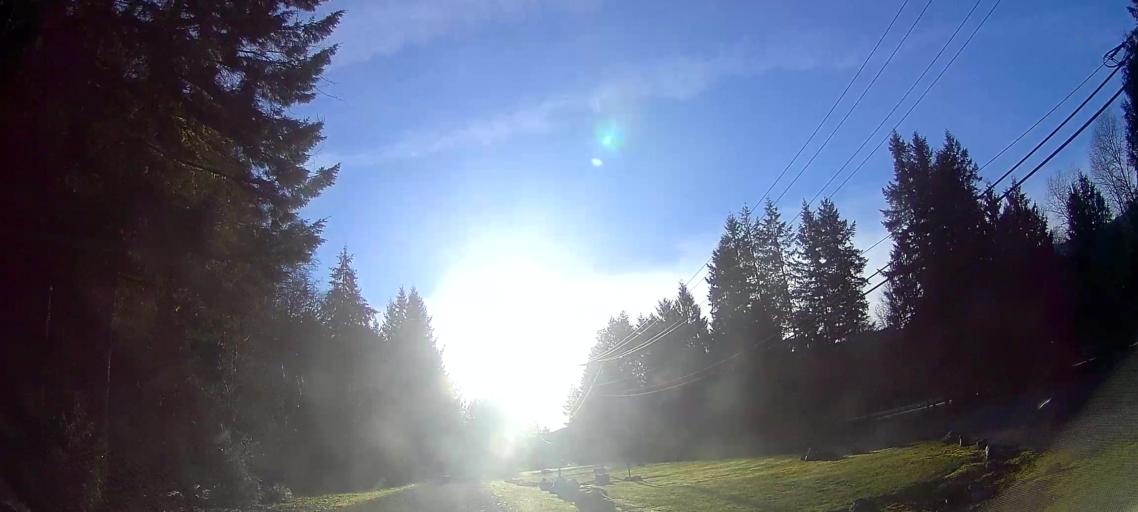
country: US
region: Washington
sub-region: Snohomish County
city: Darrington
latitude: 48.6554
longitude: -121.6910
